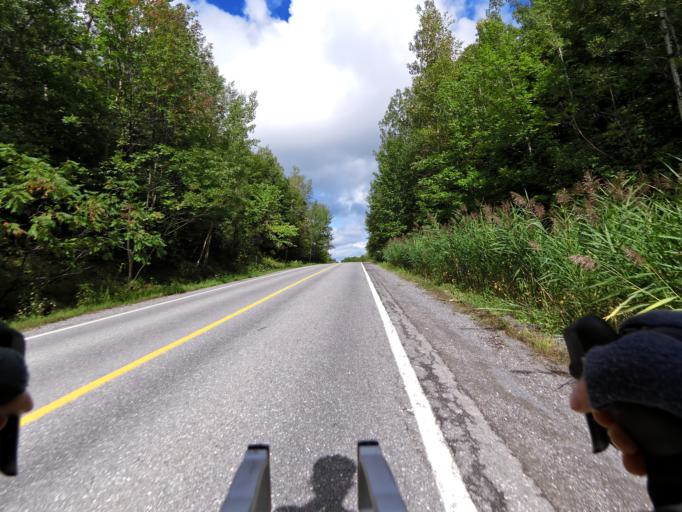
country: CA
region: Quebec
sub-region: Outaouais
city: Gatineau
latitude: 45.5039
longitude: -75.7429
